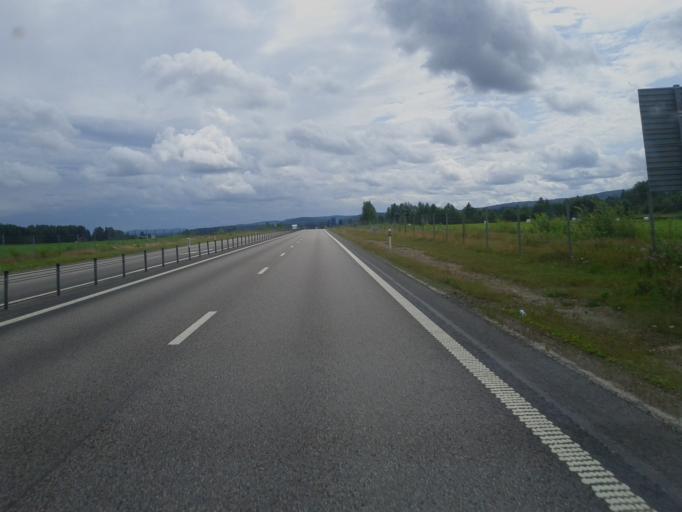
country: SE
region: Dalarna
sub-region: Borlange Kommun
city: Ornas
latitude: 60.4312
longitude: 15.5222
